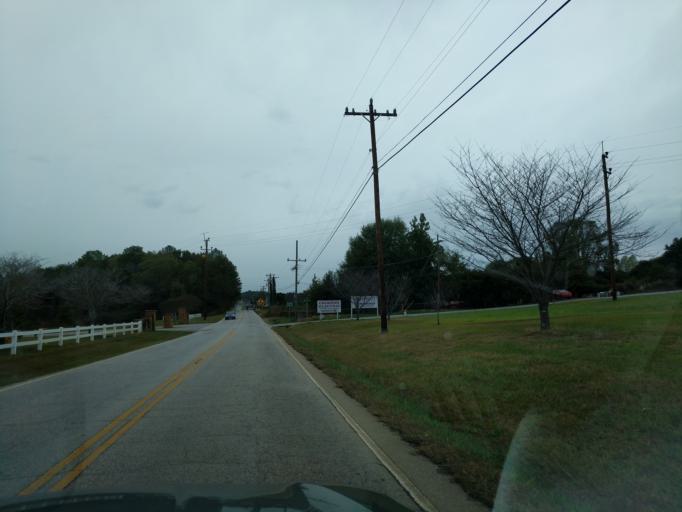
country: US
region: South Carolina
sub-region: Spartanburg County
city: Duncan
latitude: 34.9531
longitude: -82.1670
